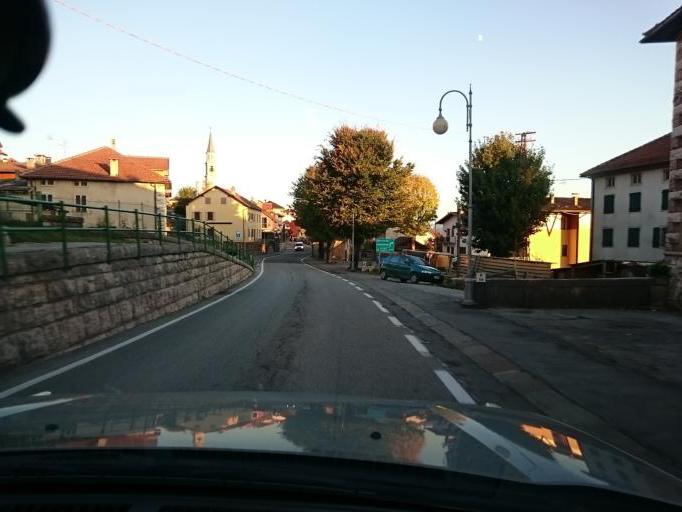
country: IT
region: Veneto
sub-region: Provincia di Vicenza
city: Canove di Roana
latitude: 45.8810
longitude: 11.4819
